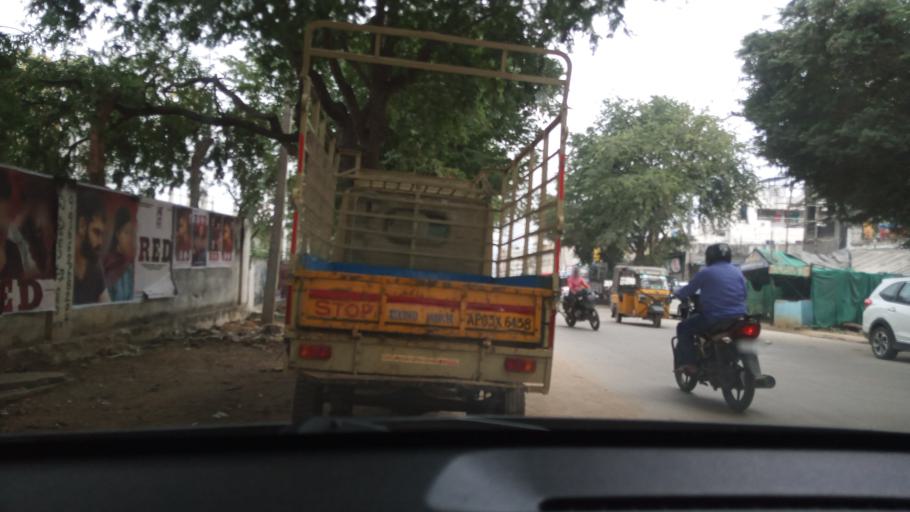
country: IN
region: Andhra Pradesh
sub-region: Chittoor
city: Madanapalle
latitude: 13.6530
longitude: 78.8026
